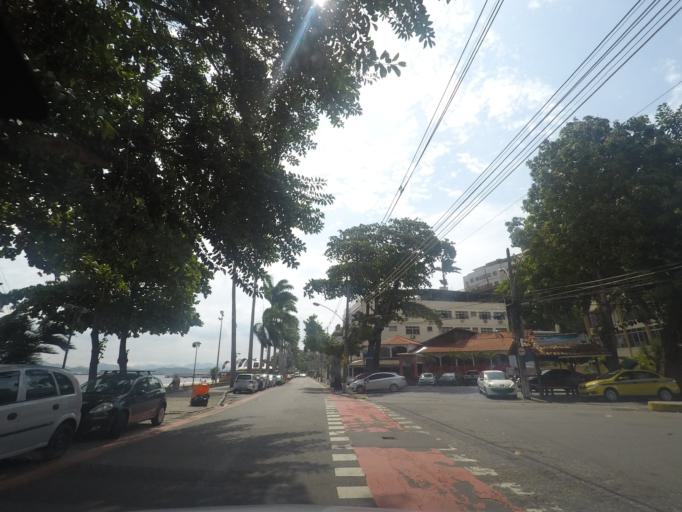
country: BR
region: Rio de Janeiro
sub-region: Rio De Janeiro
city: Rio de Janeiro
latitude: -22.8184
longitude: -43.1970
